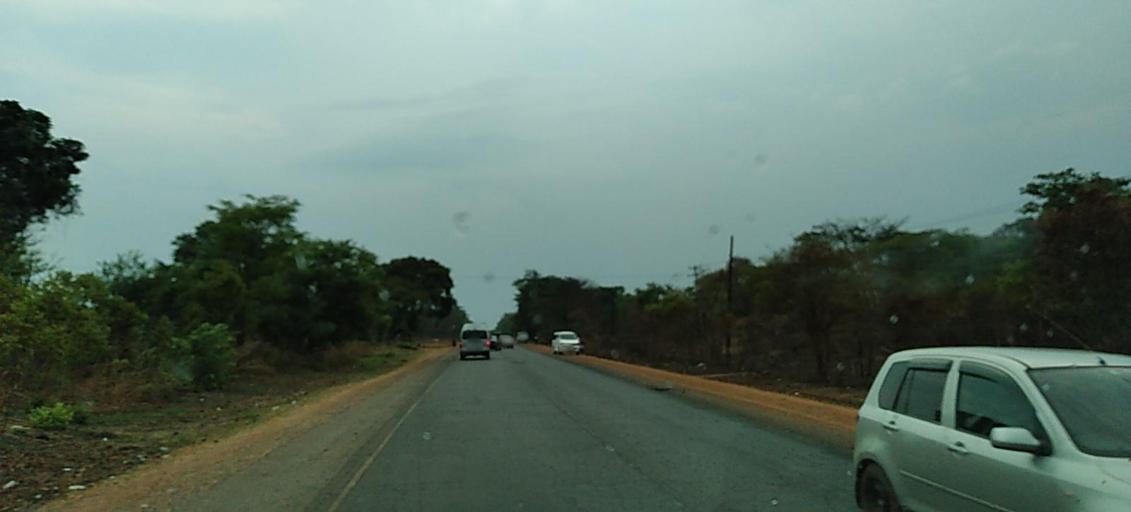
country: ZM
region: Copperbelt
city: Luanshya
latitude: -13.0822
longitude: 28.4437
